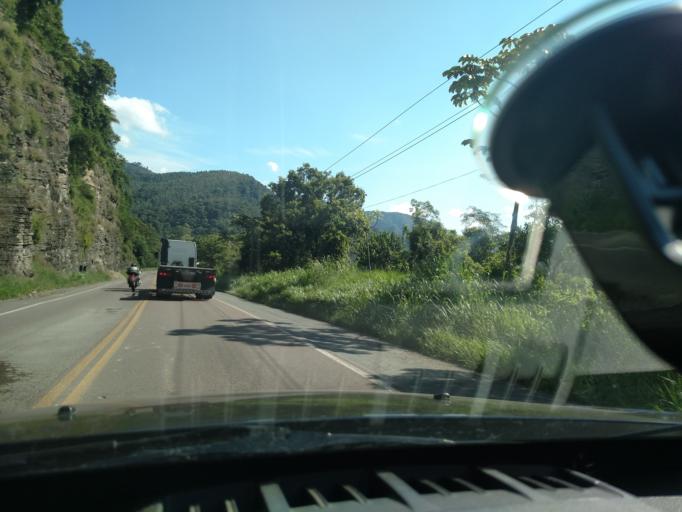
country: BR
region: Santa Catarina
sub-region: Ibirama
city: Ibirama
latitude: -27.0673
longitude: -49.4183
